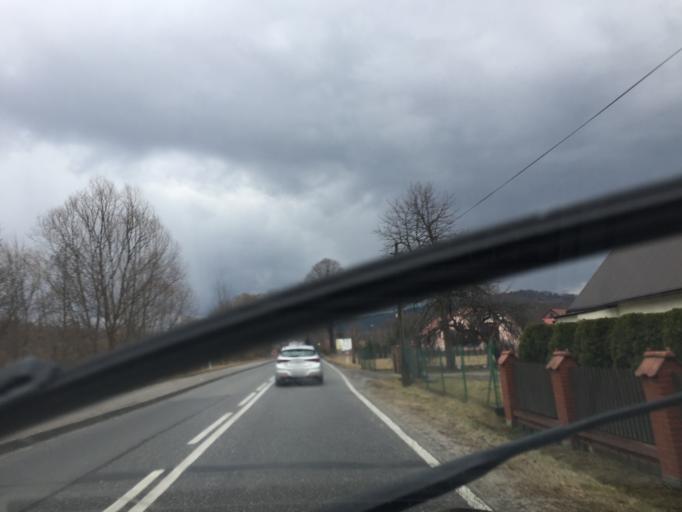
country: PL
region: Lesser Poland Voivodeship
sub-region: Powiat suski
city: Budzow
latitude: 49.7736
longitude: 19.6646
